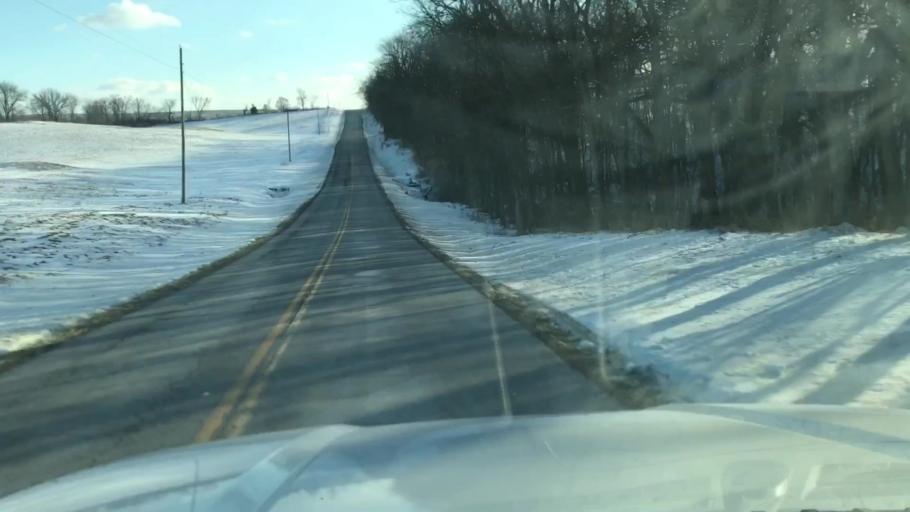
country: US
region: Missouri
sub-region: Holt County
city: Oregon
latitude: 40.0680
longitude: -94.9748
